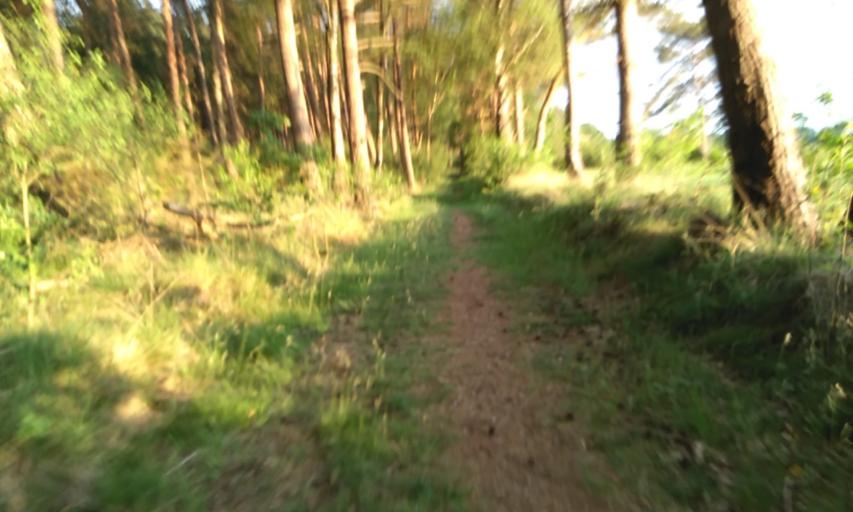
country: DE
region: Lower Saxony
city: Agathenburg
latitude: 53.5284
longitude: 9.4984
